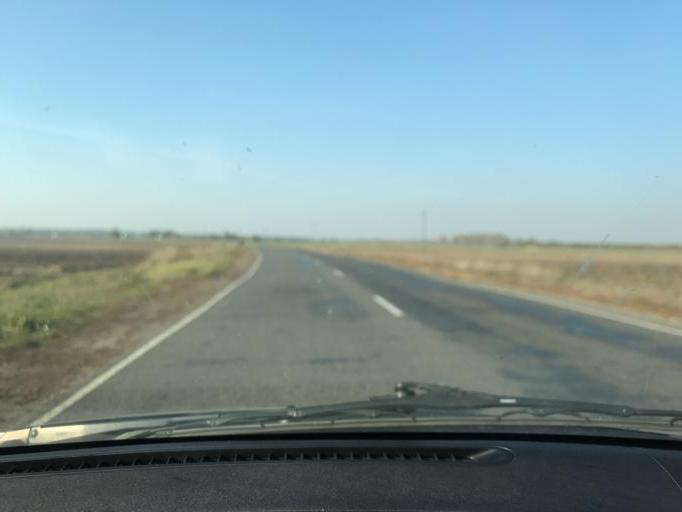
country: BY
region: Brest
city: Davyd-Haradok
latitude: 52.0667
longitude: 27.2521
